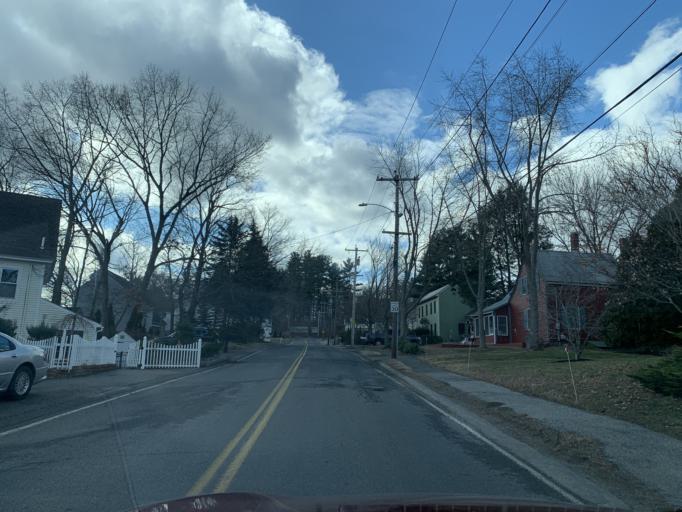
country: US
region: Massachusetts
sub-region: Essex County
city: Amesbury
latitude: 42.8358
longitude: -70.9304
